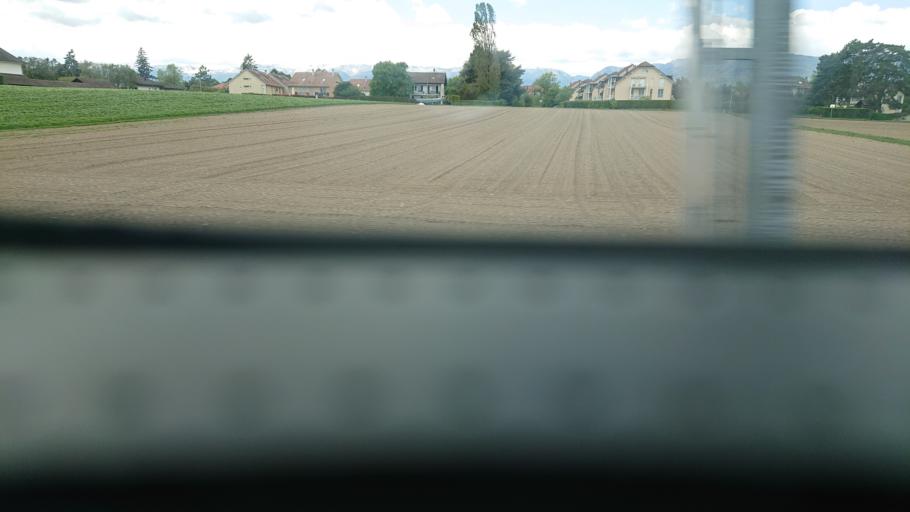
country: CH
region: Vaud
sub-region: Nyon District
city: Coppet
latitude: 46.3150
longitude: 6.1869
